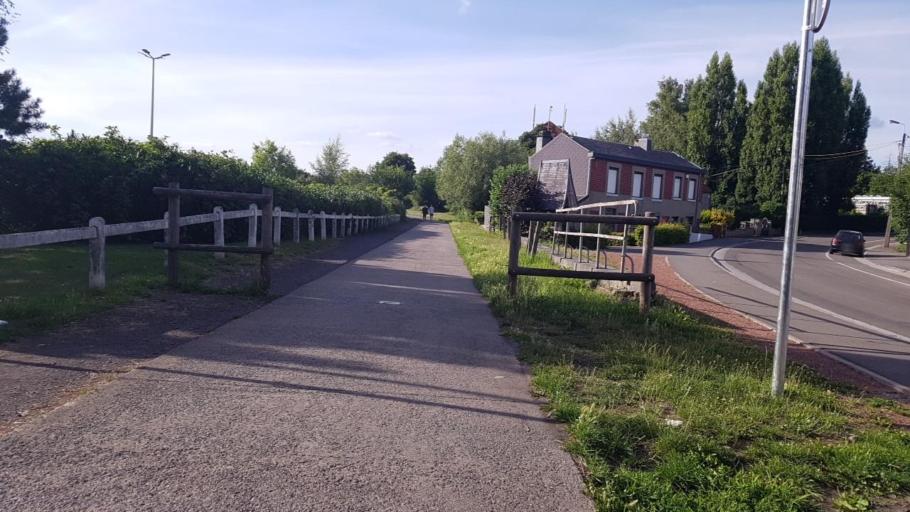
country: BE
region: Wallonia
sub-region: Province de Liege
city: Herstal
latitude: 50.6304
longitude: 5.6239
